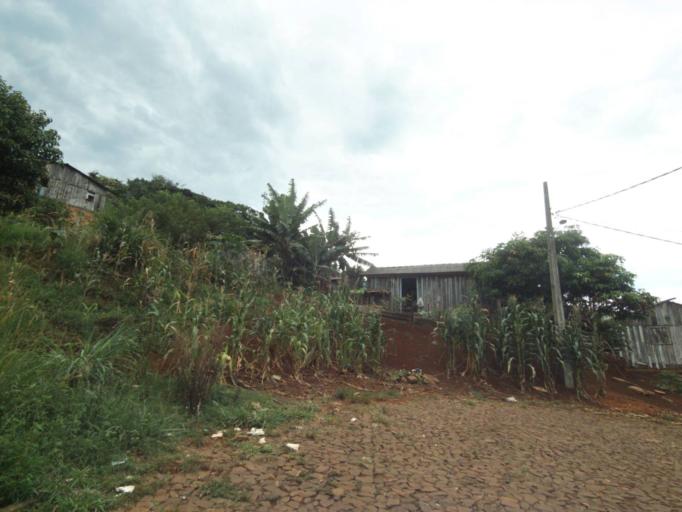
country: BR
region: Parana
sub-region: Guaraniacu
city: Guaraniacu
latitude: -25.0945
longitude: -52.8716
